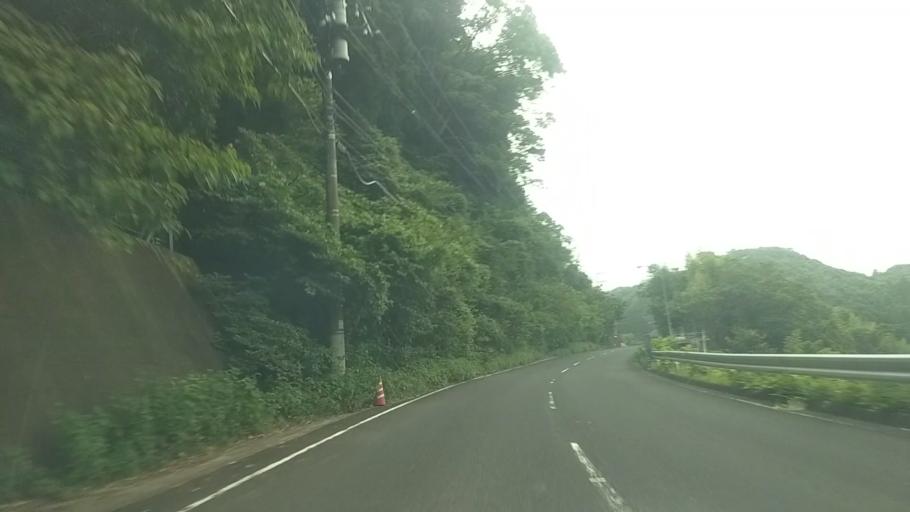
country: JP
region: Chiba
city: Katsuura
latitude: 35.2477
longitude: 140.2412
